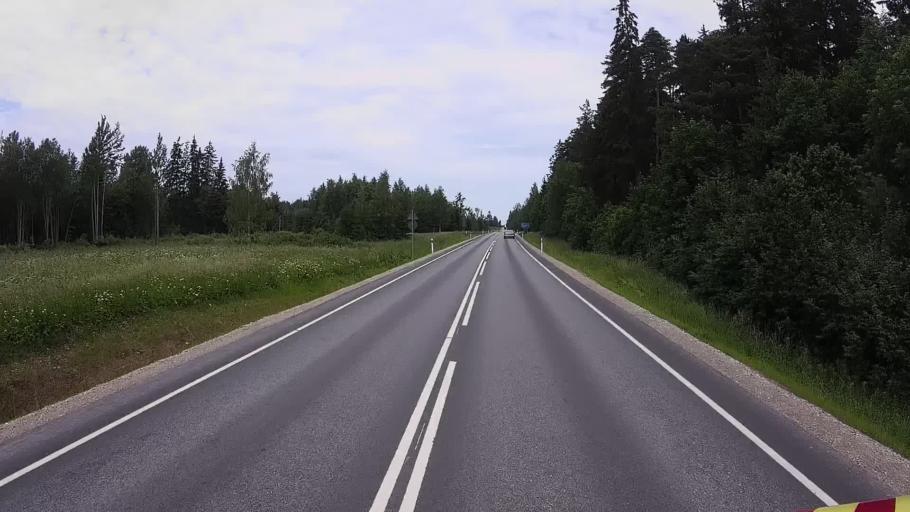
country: EE
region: Viljandimaa
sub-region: Viljandi linn
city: Viljandi
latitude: 58.2485
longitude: 25.5919
